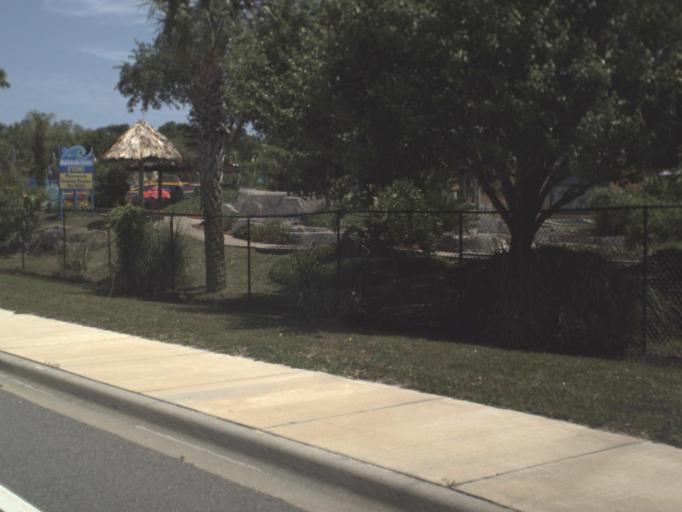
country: US
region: Florida
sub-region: Duval County
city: Jacksonville Beach
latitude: 30.2880
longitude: -81.4120
